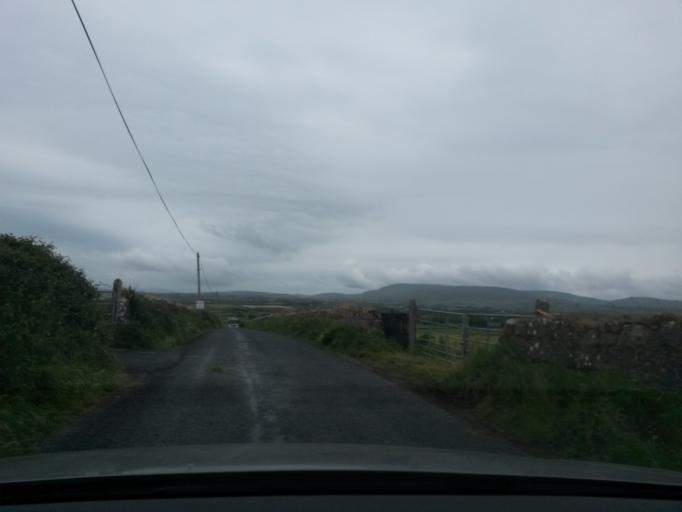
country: IE
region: Connaught
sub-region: Sligo
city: Inishcrone
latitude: 54.2563
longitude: -8.8807
